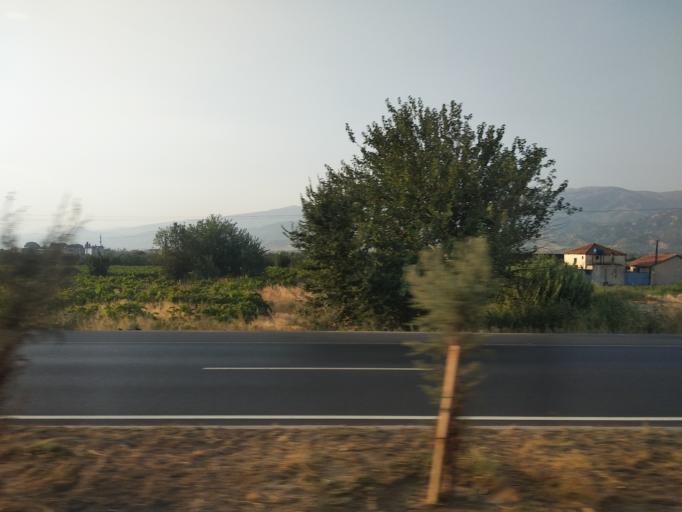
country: TR
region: Manisa
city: Salihli
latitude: 38.4976
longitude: 28.1924
